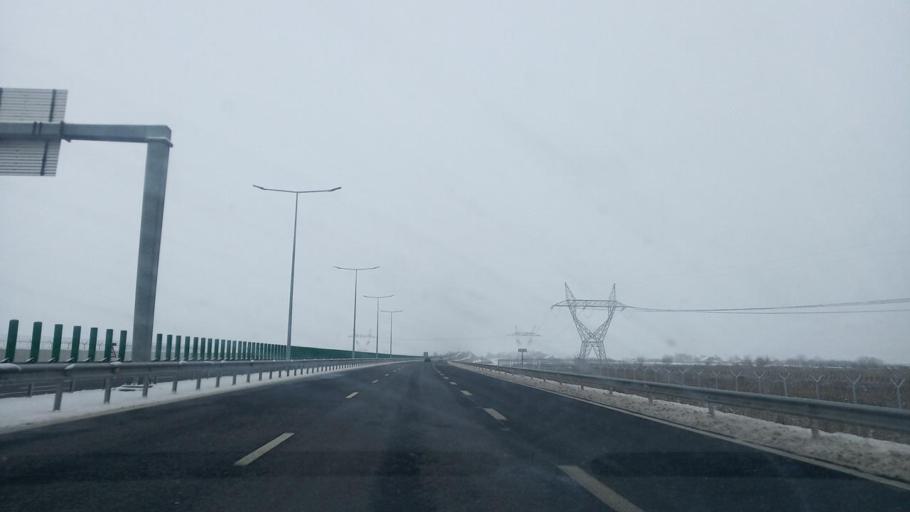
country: RO
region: Bacau
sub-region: Comuna Letea Veche
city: Holt
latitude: 46.5913
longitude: 26.9613
